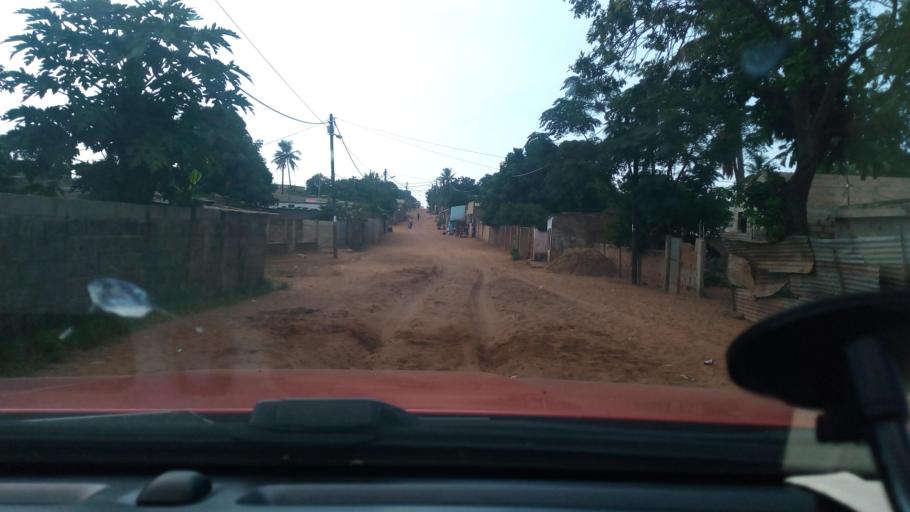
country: MZ
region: Maputo City
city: Maputo
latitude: -25.9208
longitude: 32.5970
